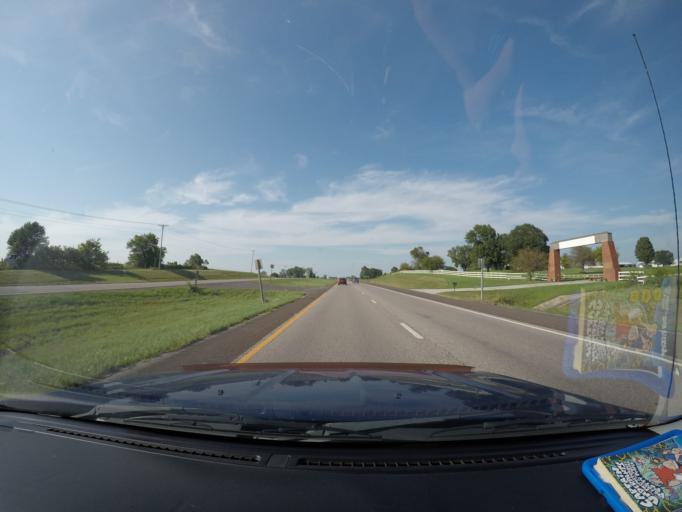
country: US
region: Kansas
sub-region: Leavenworth County
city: Basehor
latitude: 39.1531
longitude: -94.9007
